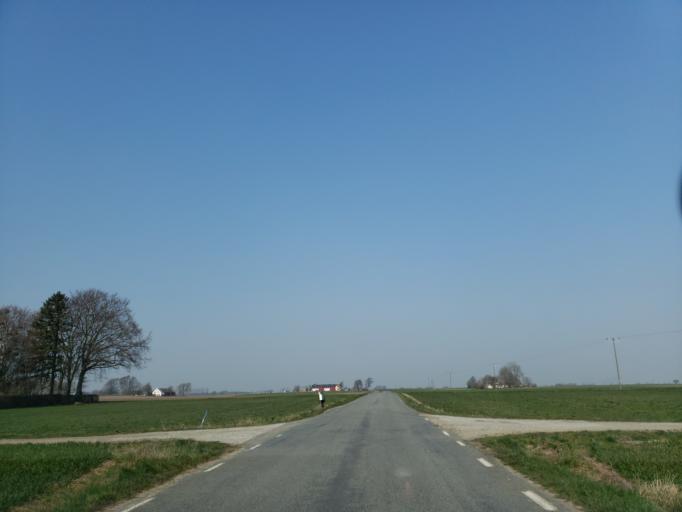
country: SE
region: Skane
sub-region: Simrishamns Kommun
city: Simrishamn
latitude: 55.4526
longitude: 14.2152
